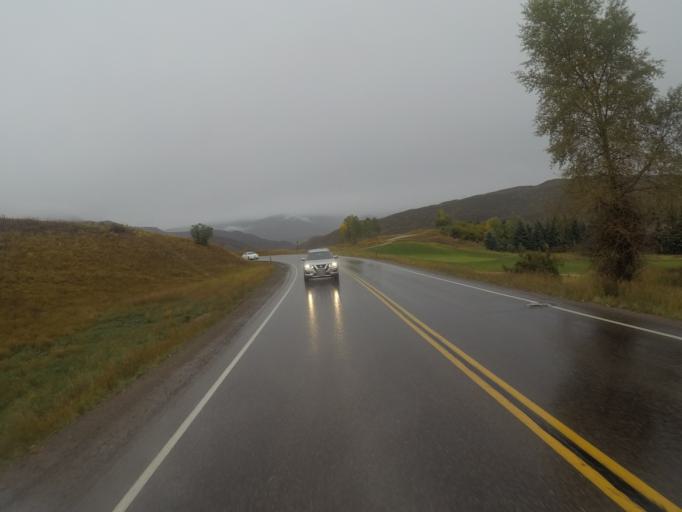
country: US
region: Colorado
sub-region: Pitkin County
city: Snowmass Village
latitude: 39.2189
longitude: -106.9323
